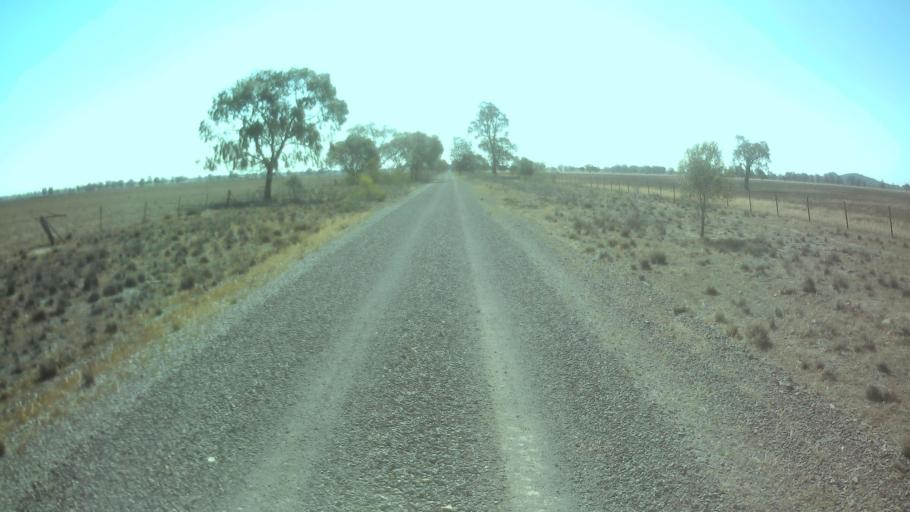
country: AU
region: New South Wales
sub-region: Weddin
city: Grenfell
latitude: -33.7600
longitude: 147.7097
